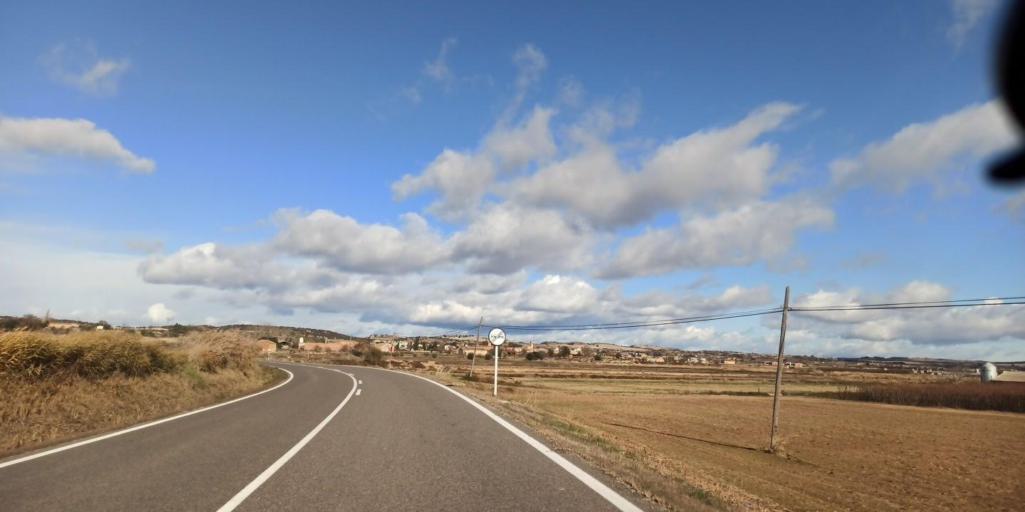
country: ES
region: Catalonia
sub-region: Provincia de Lleida
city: Penelles
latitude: 41.7491
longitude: 0.9543
